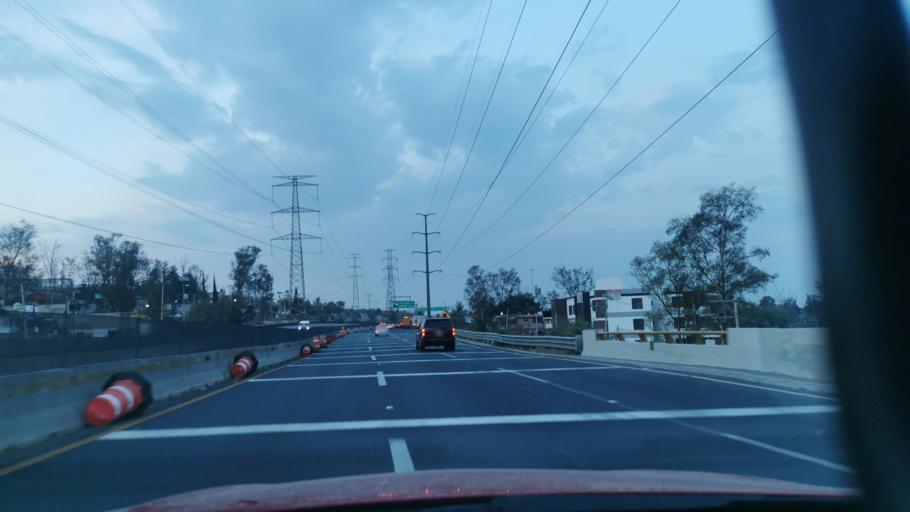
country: MX
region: Mexico
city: Cuautitlan Izcalli
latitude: 19.6119
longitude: -99.2340
